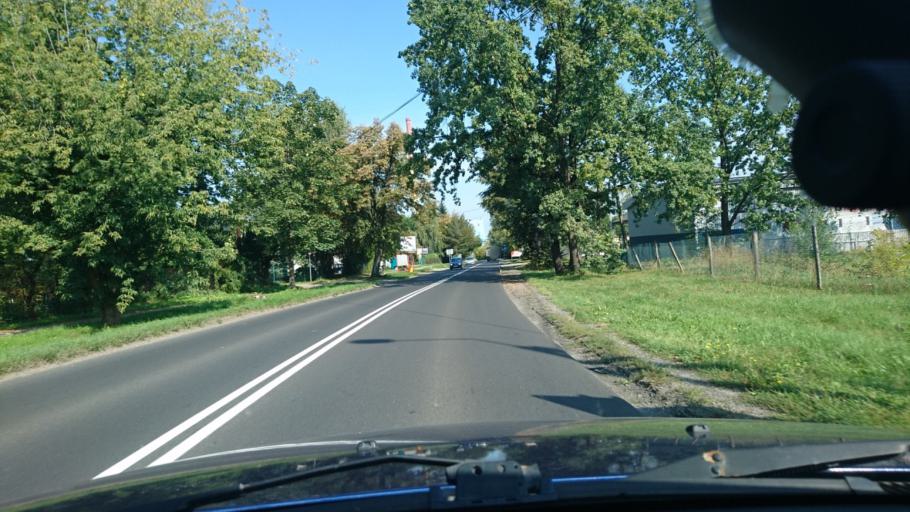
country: PL
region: Silesian Voivodeship
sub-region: Powiat bielski
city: Bestwina
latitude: 49.8650
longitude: 19.0297
